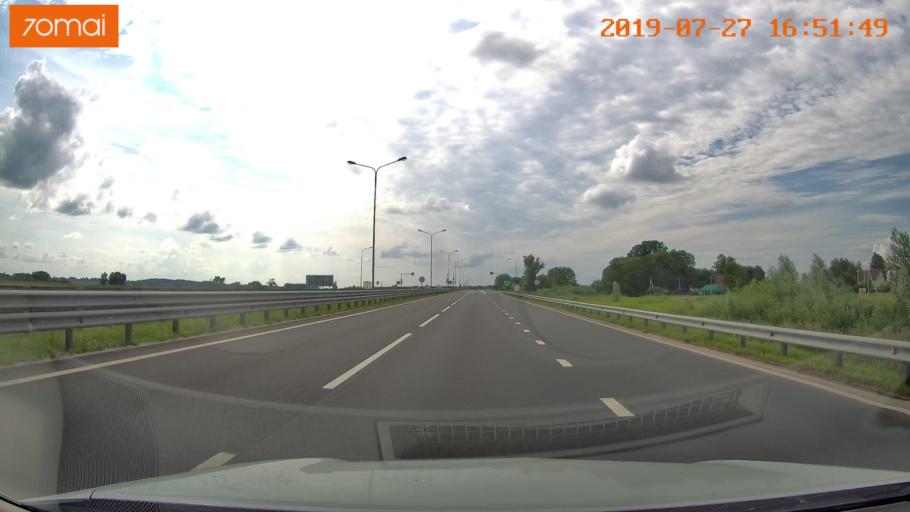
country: RU
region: Kaliningrad
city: Gvardeysk
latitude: 54.6840
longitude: 20.8755
